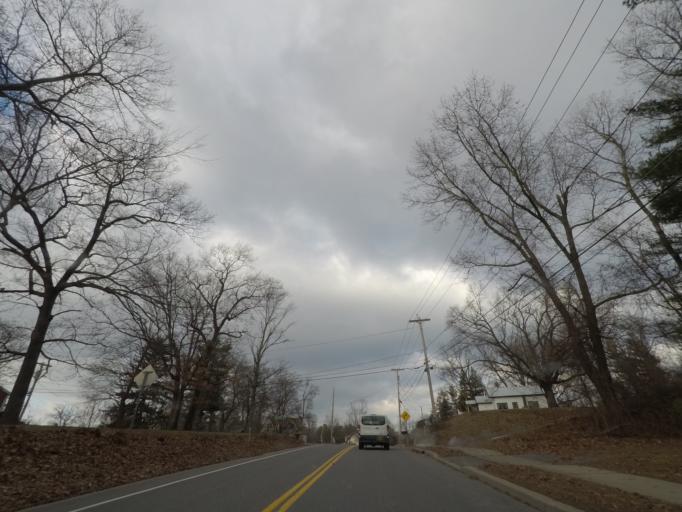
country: US
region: New York
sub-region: Albany County
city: Westmere
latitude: 42.6819
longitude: -73.8725
